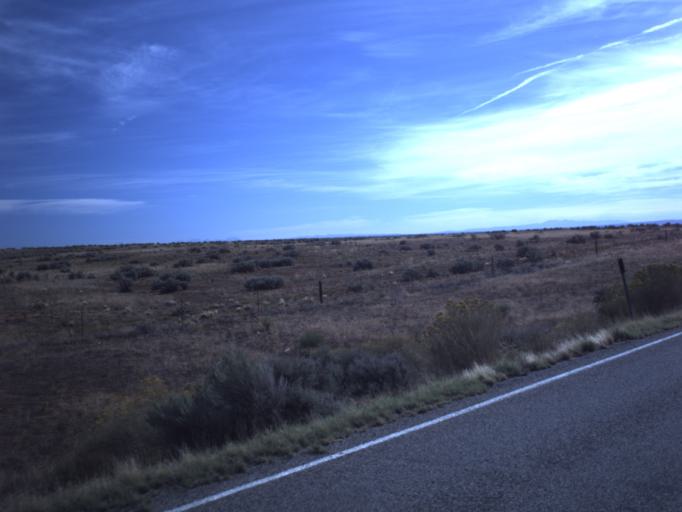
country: US
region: Utah
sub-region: San Juan County
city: Blanding
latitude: 37.4318
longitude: -109.3666
